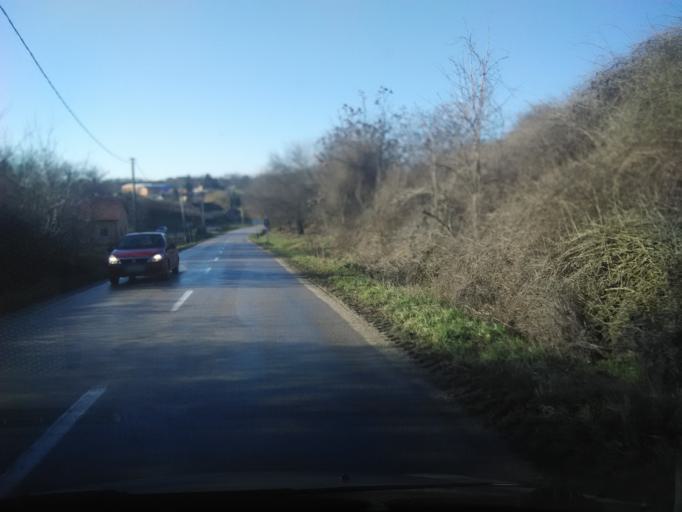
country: SK
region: Nitriansky
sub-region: Okres Nitra
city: Vrable
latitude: 48.2318
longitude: 18.2317
